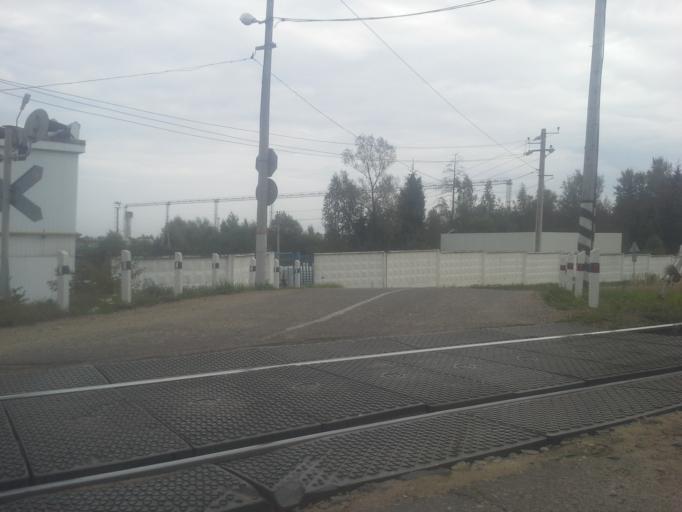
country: RU
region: Moskovskaya
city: Kievskij
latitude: 55.4012
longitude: 36.8889
